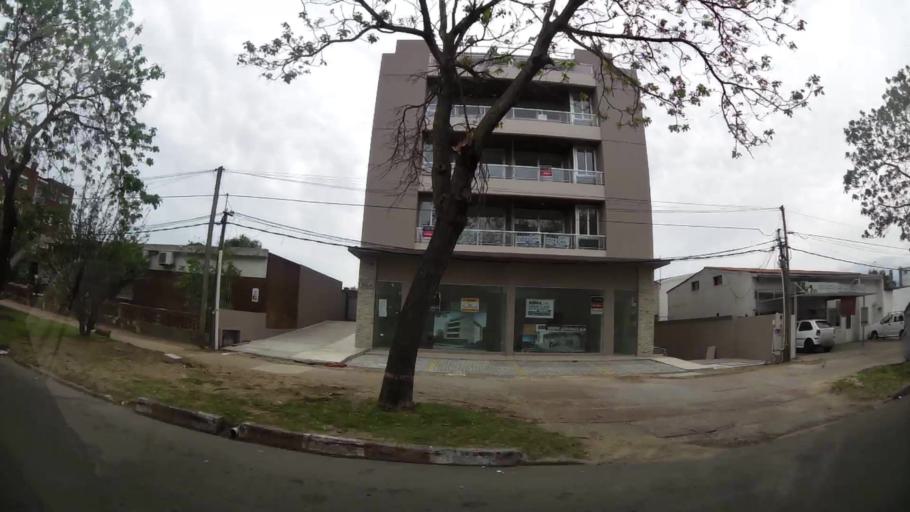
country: UY
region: Maldonado
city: Maldonado
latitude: -34.9062
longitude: -54.9634
